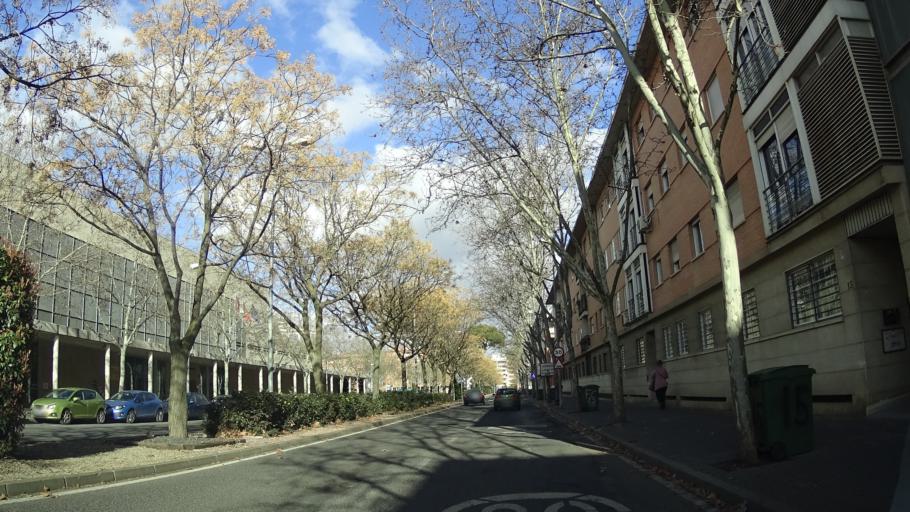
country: ES
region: Castille-La Mancha
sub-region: Provincia de Ciudad Real
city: Ciudad Real
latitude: 38.9790
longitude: -3.9336
